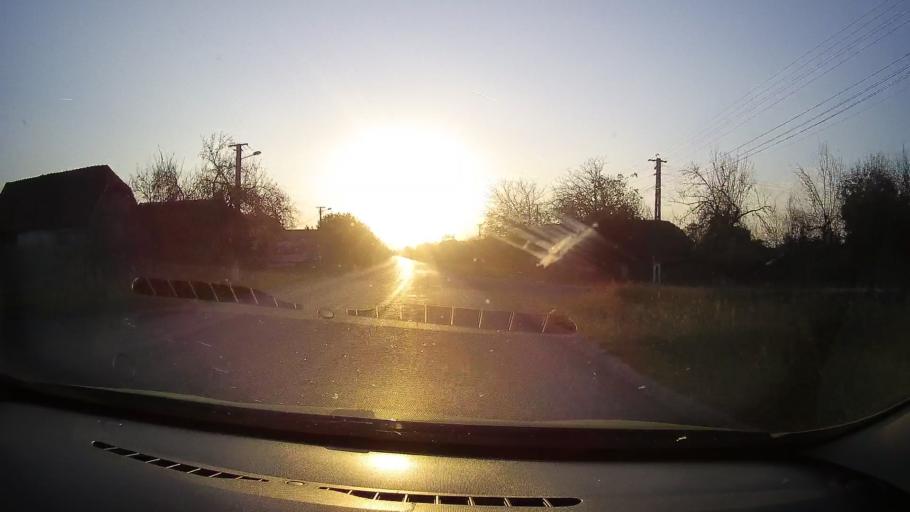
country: RO
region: Arad
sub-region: Comuna Ineu
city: Ineu
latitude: 46.4328
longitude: 21.8471
